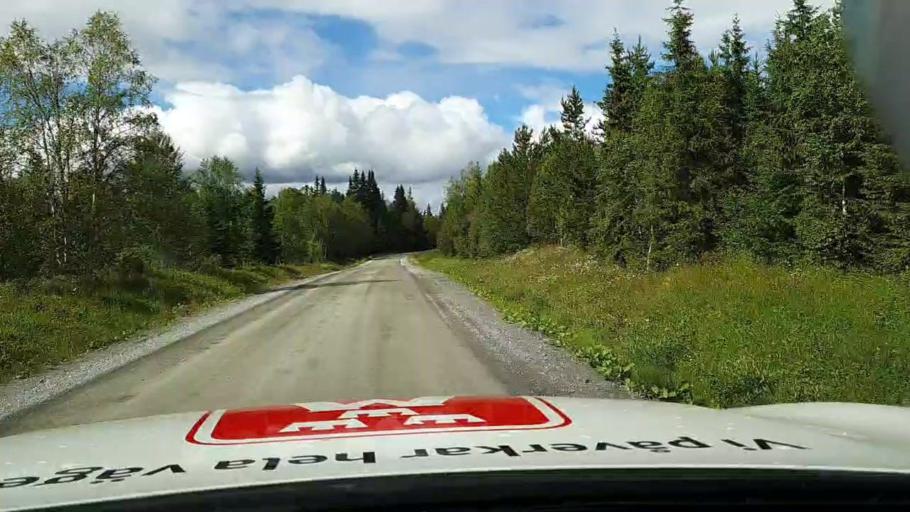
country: SE
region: Jaemtland
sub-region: Krokoms Kommun
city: Valla
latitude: 63.6777
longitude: 13.6821
